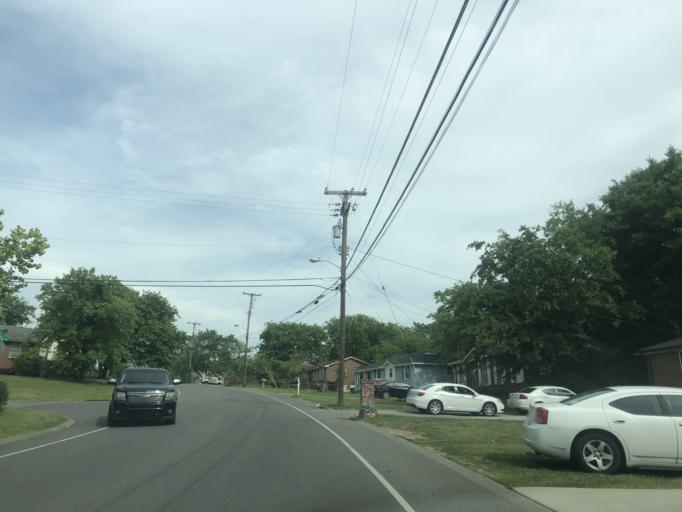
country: US
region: Tennessee
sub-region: Davidson County
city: Nashville
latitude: 36.2223
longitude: -86.8087
